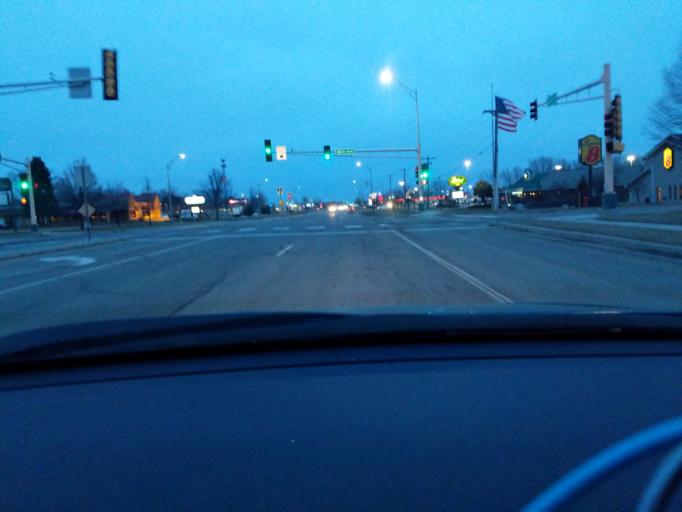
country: US
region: Minnesota
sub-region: Kandiyohi County
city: Willmar
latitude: 45.0958
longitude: -95.0425
